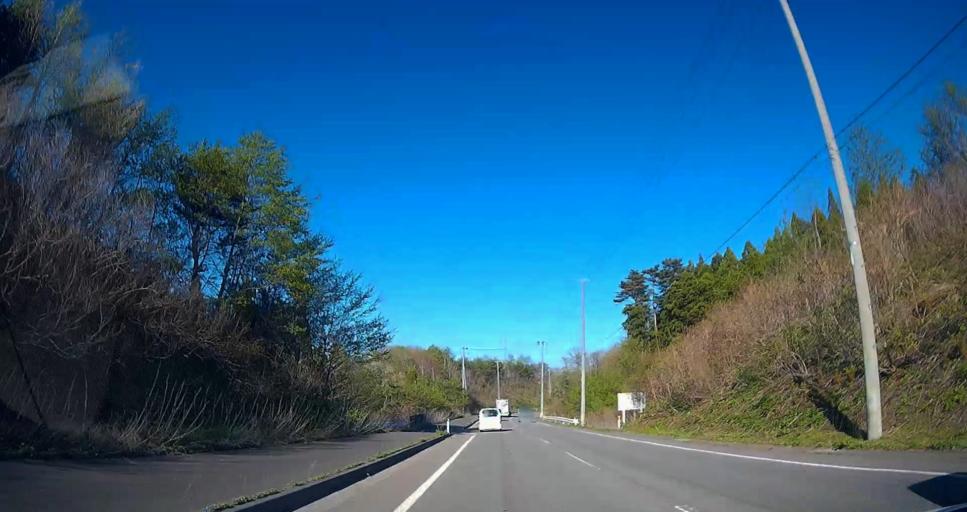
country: JP
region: Aomori
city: Mutsu
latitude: 41.4303
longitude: 141.1421
